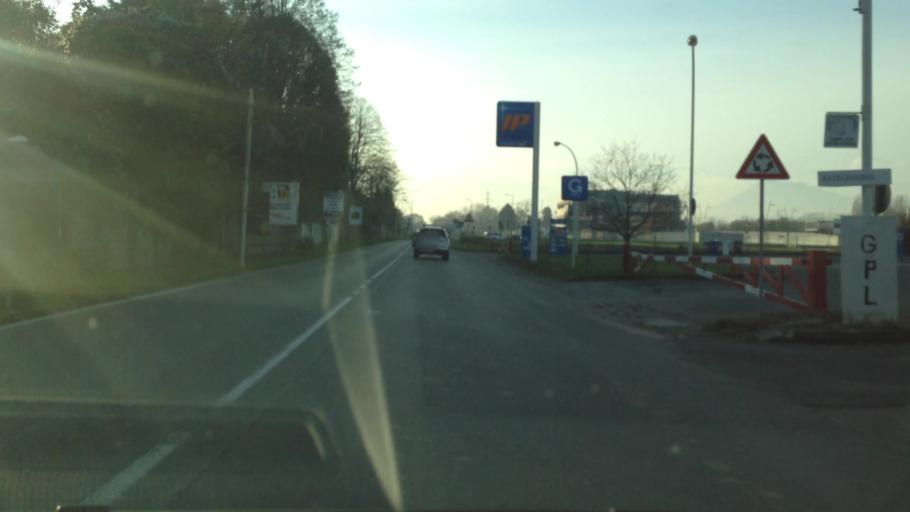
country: IT
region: Piedmont
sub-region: Provincia di Torino
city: Savonera
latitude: 45.0988
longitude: 7.6090
